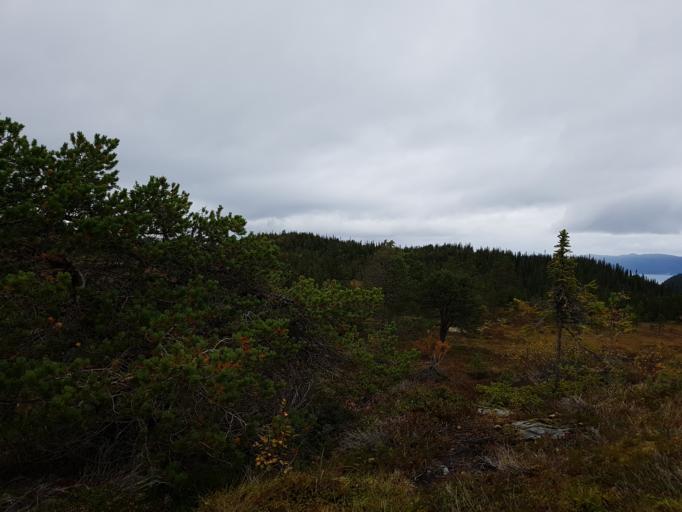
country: NO
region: Sor-Trondelag
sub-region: Melhus
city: Melhus
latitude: 63.4167
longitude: 10.2180
